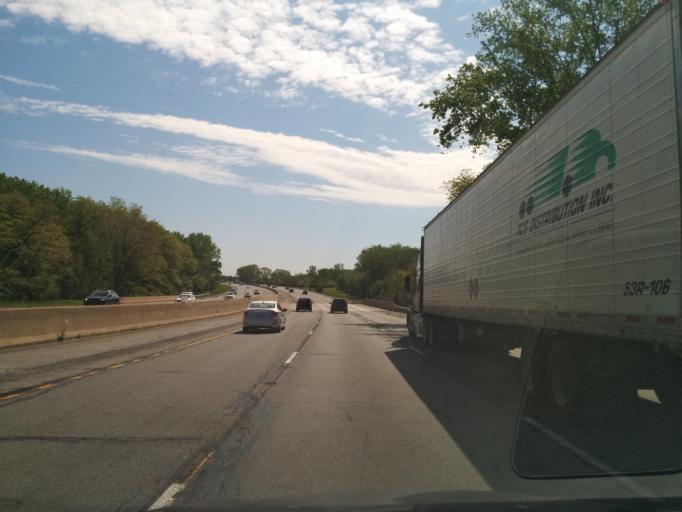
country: US
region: Indiana
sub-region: Porter County
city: Burns Harbor
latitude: 41.6016
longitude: -87.1493
